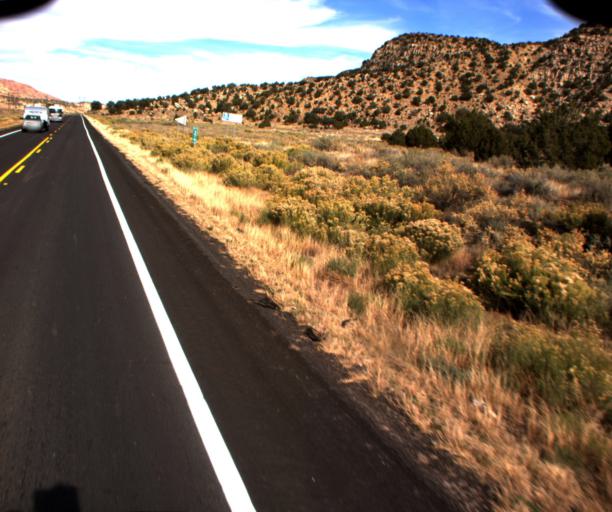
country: US
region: Arizona
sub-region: Navajo County
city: Kayenta
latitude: 36.6156
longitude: -110.4690
